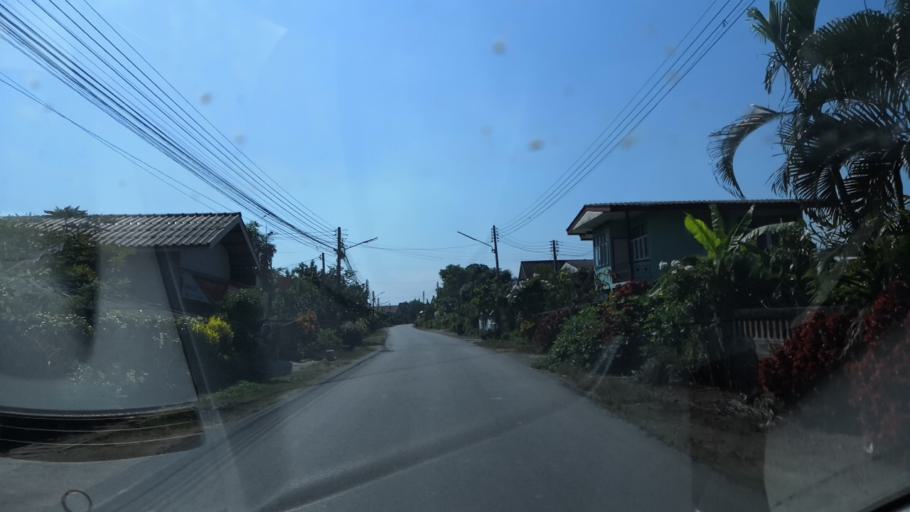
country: TH
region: Chiang Rai
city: Wiang Chai
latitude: 19.8890
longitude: 99.9497
